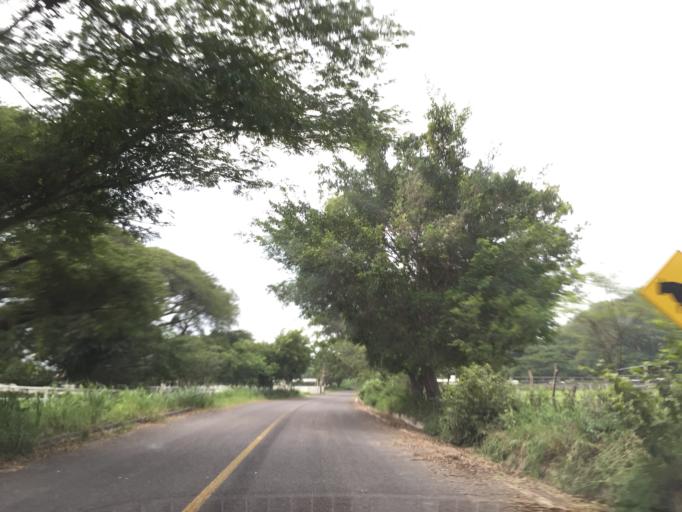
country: MX
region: Colima
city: Comala
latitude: 19.3980
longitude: -103.8031
